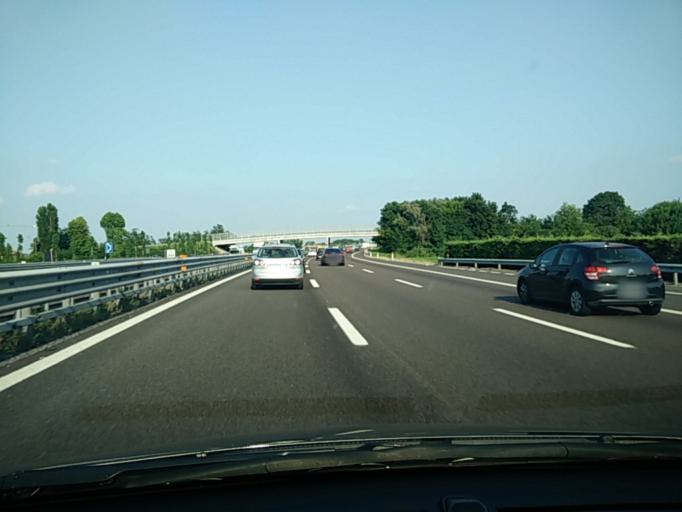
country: IT
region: Veneto
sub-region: Provincia di Vicenza
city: Arcugnano-Torri
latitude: 45.5169
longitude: 11.5824
